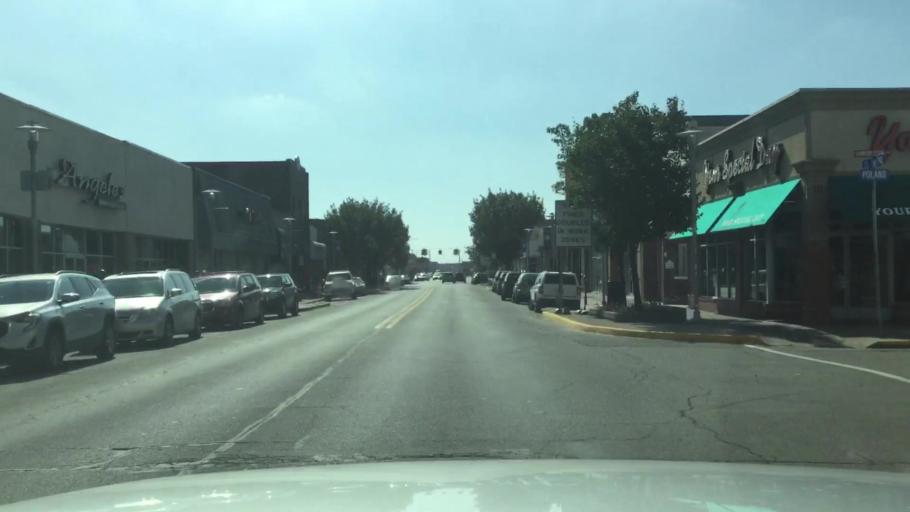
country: US
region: Michigan
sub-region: Wayne County
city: Hamtramck
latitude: 42.3953
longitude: -83.0567
